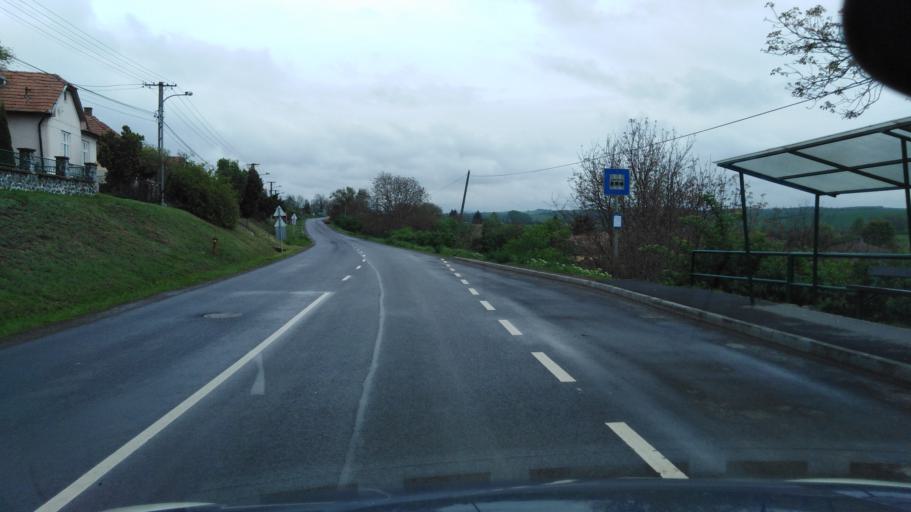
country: HU
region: Nograd
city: Karancskeszi
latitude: 48.1227
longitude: 19.6387
